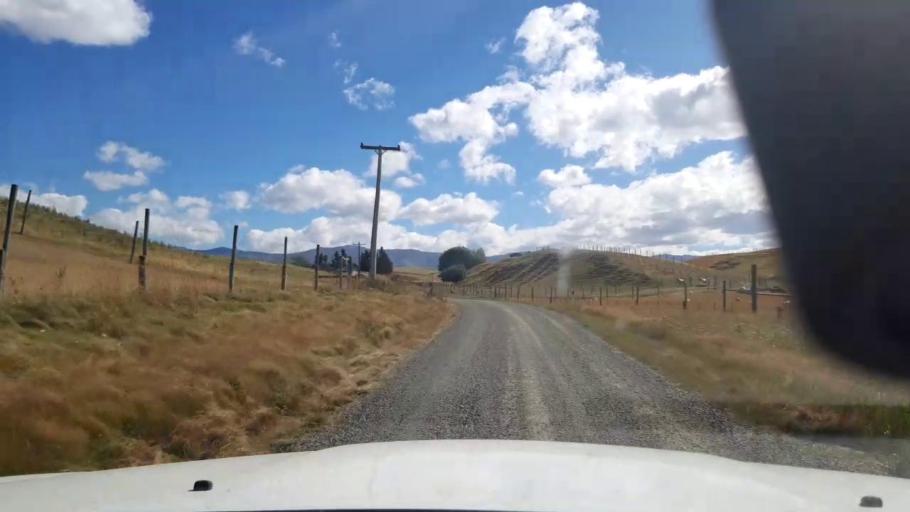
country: NZ
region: Canterbury
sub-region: Timaru District
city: Pleasant Point
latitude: -44.2353
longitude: 170.8712
